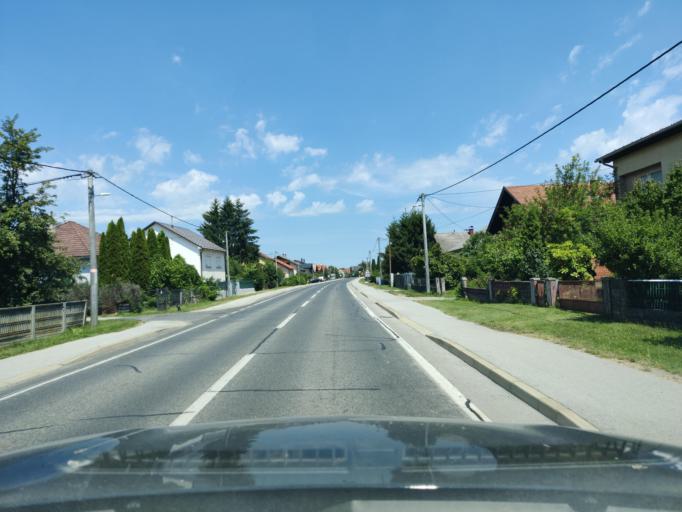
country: HR
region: Medimurska
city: Mackovec
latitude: 46.4244
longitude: 16.4285
